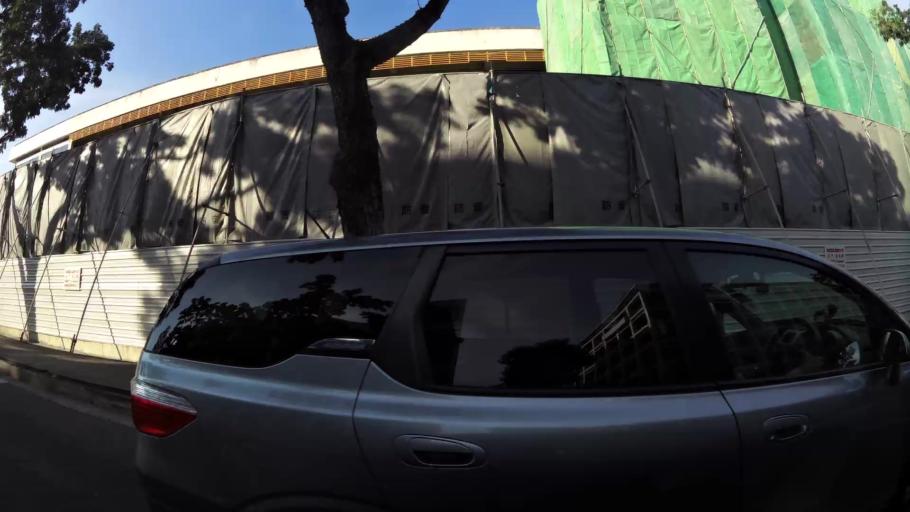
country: SG
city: Singapore
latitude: 1.3246
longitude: 103.8742
